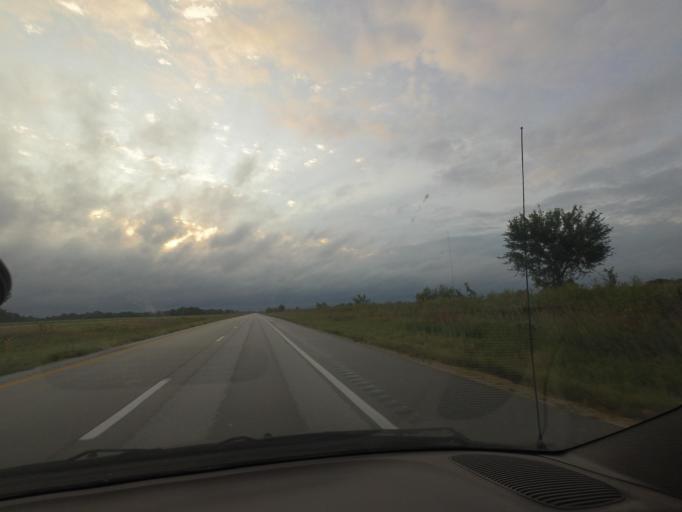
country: US
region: Missouri
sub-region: Shelby County
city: Shelbina
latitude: 39.6807
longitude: -91.9844
